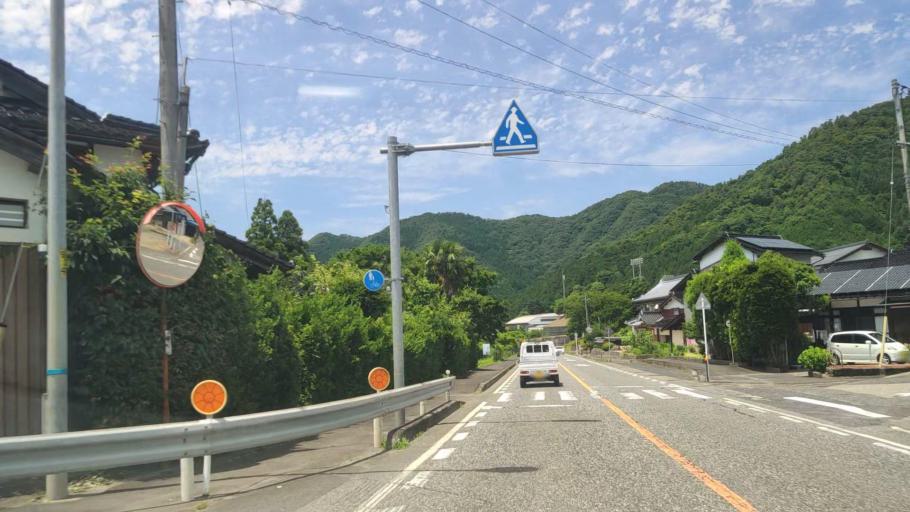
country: JP
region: Tottori
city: Tottori
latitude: 35.3637
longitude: 134.3439
